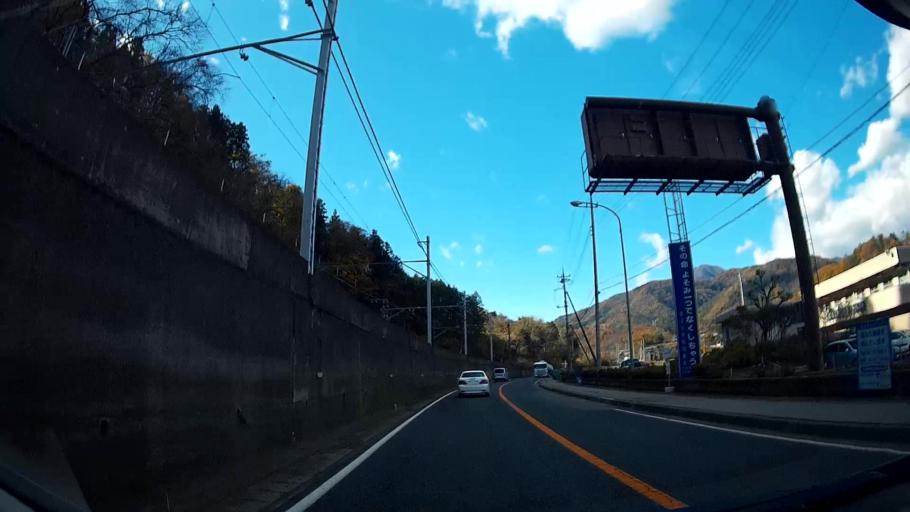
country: JP
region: Yamanashi
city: Otsuki
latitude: 35.5987
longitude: 138.9119
